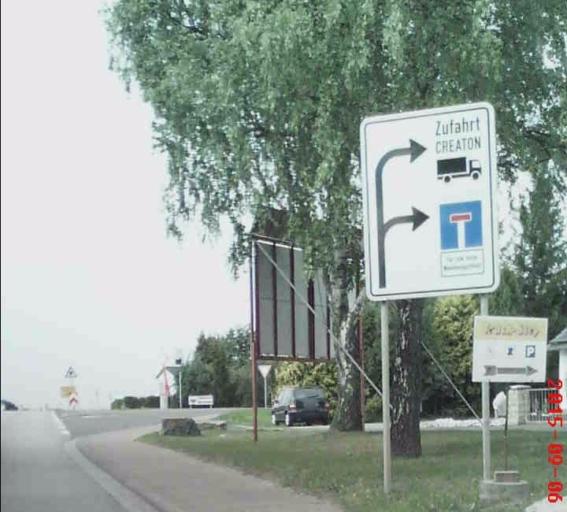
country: DE
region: Thuringia
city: Altengottern
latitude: 51.1502
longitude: 10.5613
